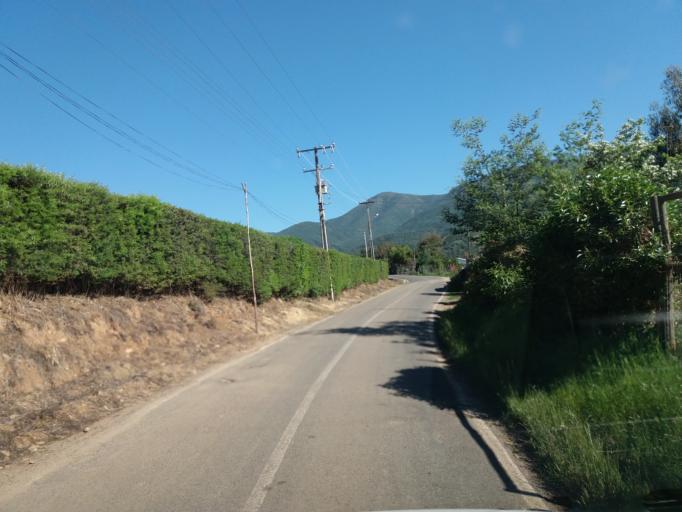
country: CL
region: Valparaiso
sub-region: Provincia de Quillota
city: Quillota
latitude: -32.8592
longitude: -71.2857
